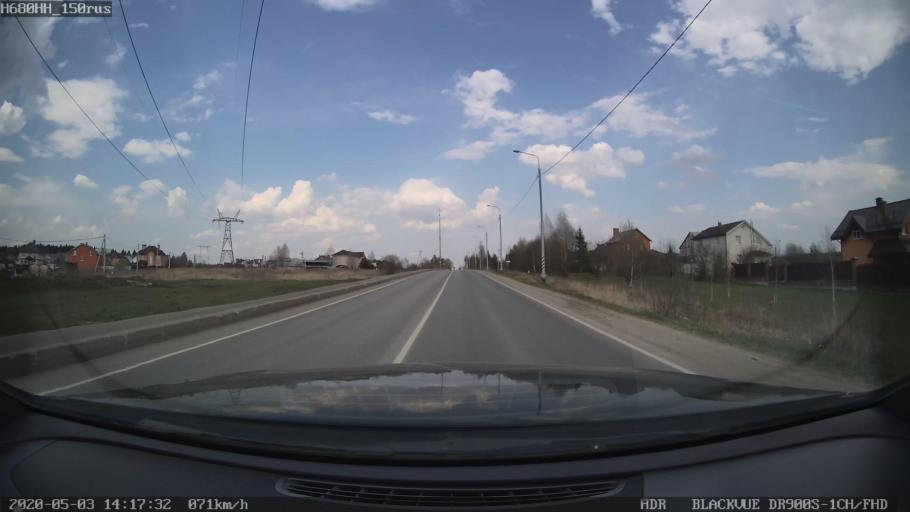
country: RU
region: Moskovskaya
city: Solnechnogorsk
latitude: 56.2098
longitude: 36.9656
